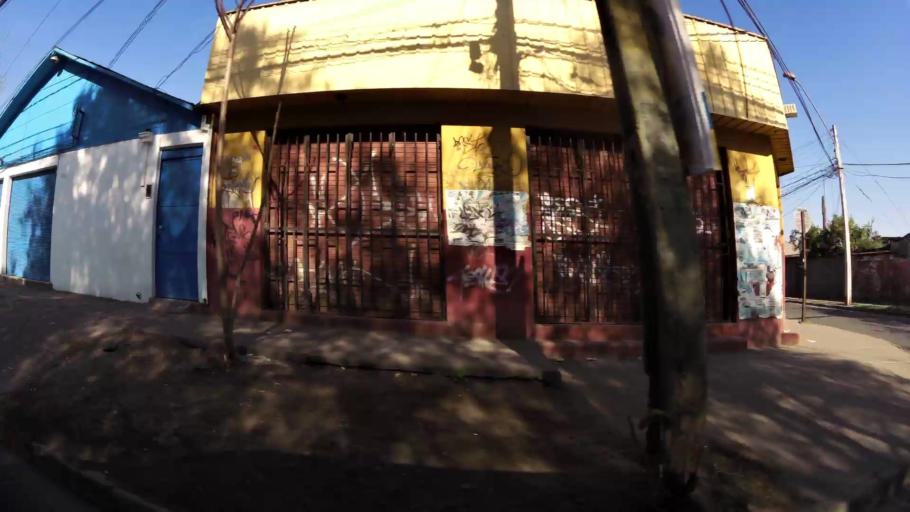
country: CL
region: Santiago Metropolitan
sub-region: Provincia de Santiago
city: Santiago
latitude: -33.3912
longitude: -70.6686
